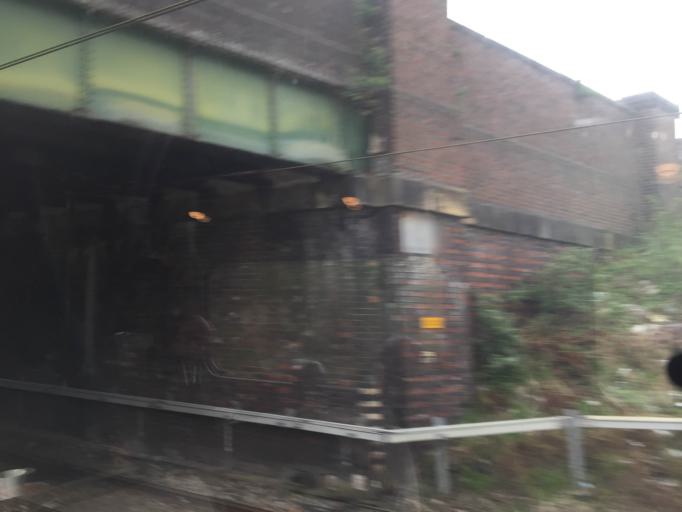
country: GB
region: England
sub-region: Warrington
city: Warrington
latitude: 53.3949
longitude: -2.6026
